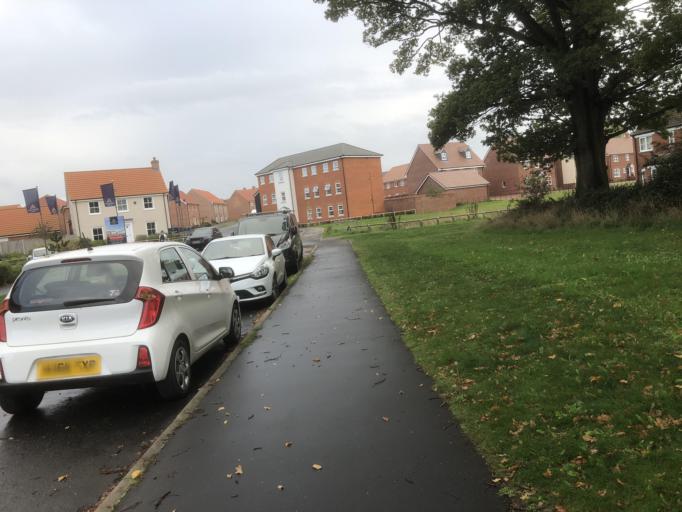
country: GB
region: England
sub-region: Norfolk
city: Spixworth
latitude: 52.6590
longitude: 1.3436
